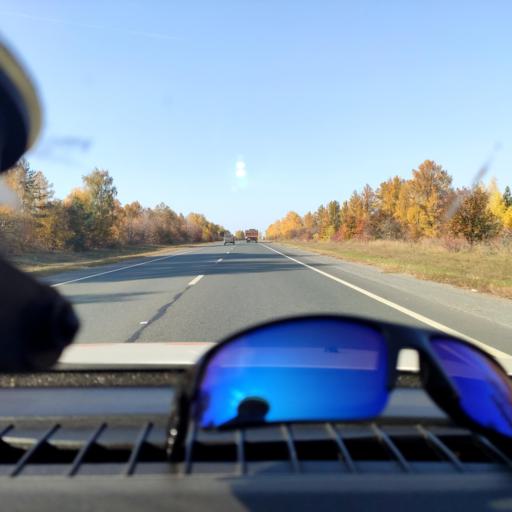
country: RU
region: Samara
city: Volzhskiy
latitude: 53.4716
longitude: 50.1221
